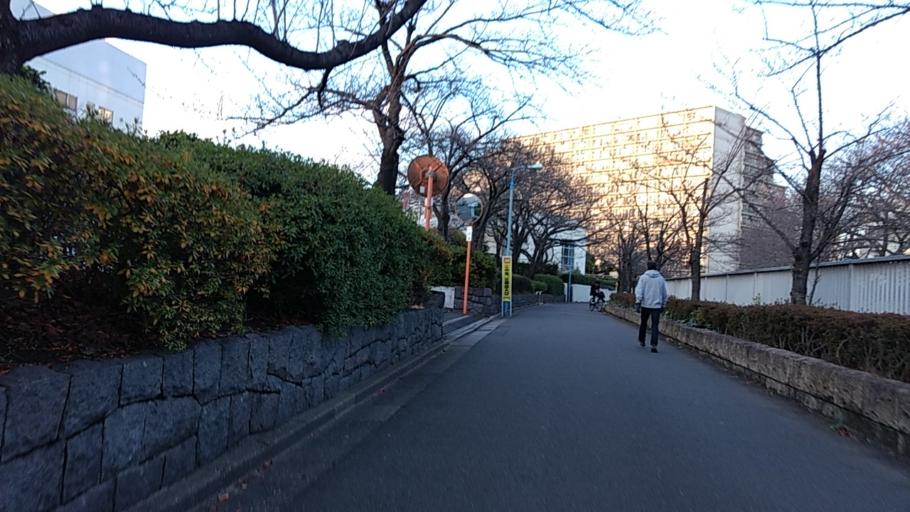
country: JP
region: Tokyo
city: Tokyo
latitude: 35.7137
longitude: 139.6947
